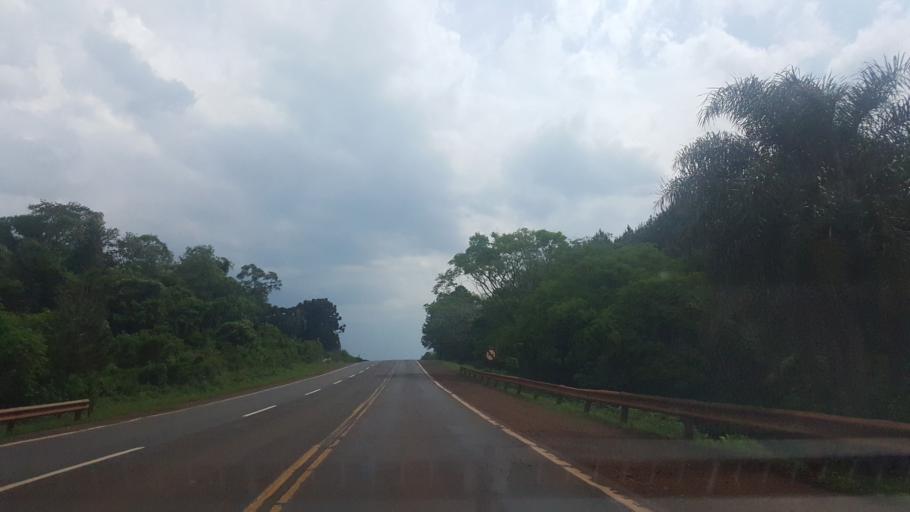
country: AR
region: Misiones
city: Jardin America
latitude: -27.1009
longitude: -55.3108
